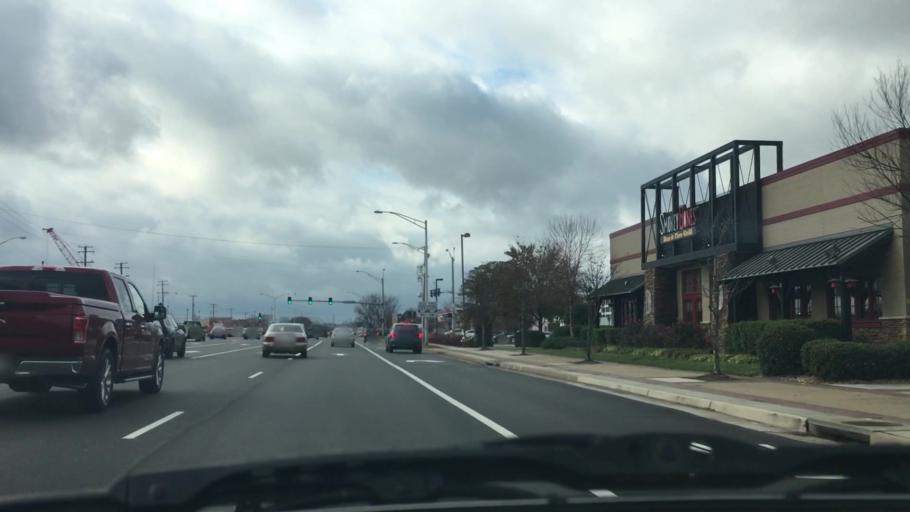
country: US
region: Virginia
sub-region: City of Chesapeake
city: Chesapeake
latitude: 36.8440
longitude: -76.1357
